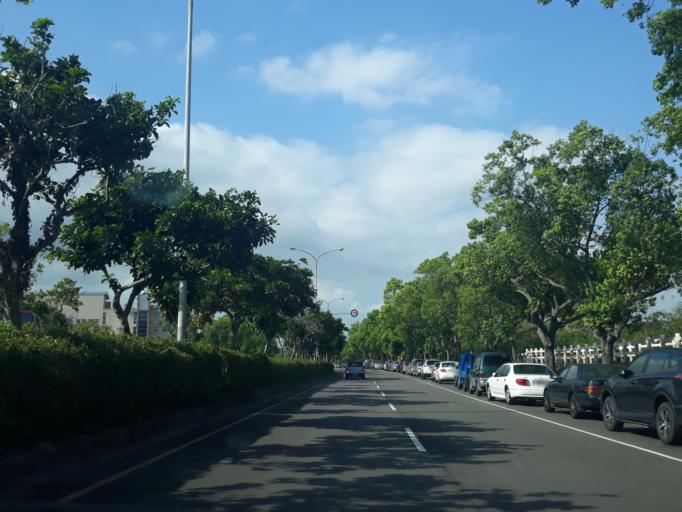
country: TW
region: Taiwan
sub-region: Miaoli
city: Miaoli
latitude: 24.5797
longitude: 120.8431
